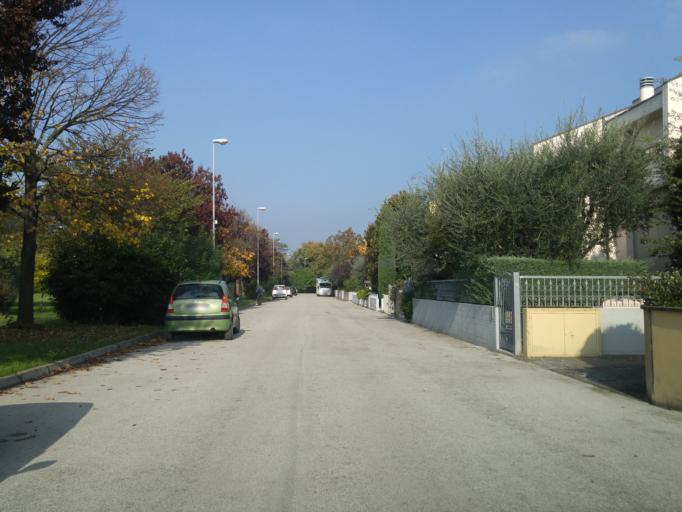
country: IT
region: The Marches
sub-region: Provincia di Pesaro e Urbino
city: Fano
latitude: 43.8289
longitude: 13.0092
